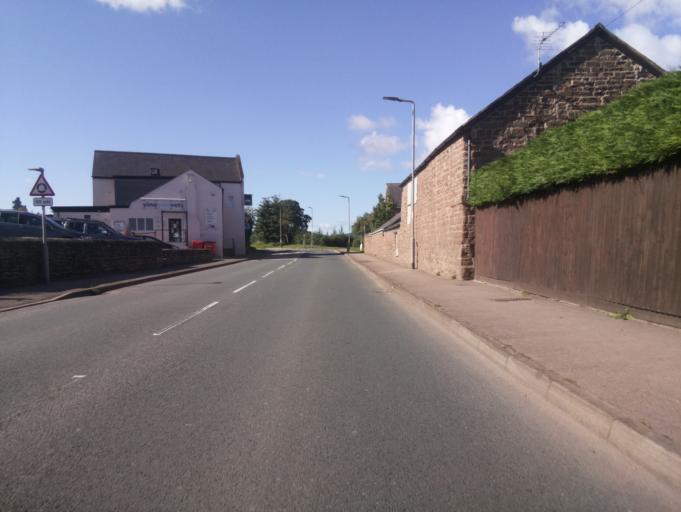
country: GB
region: England
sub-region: Herefordshire
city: Walford
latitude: 51.9012
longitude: -2.5901
